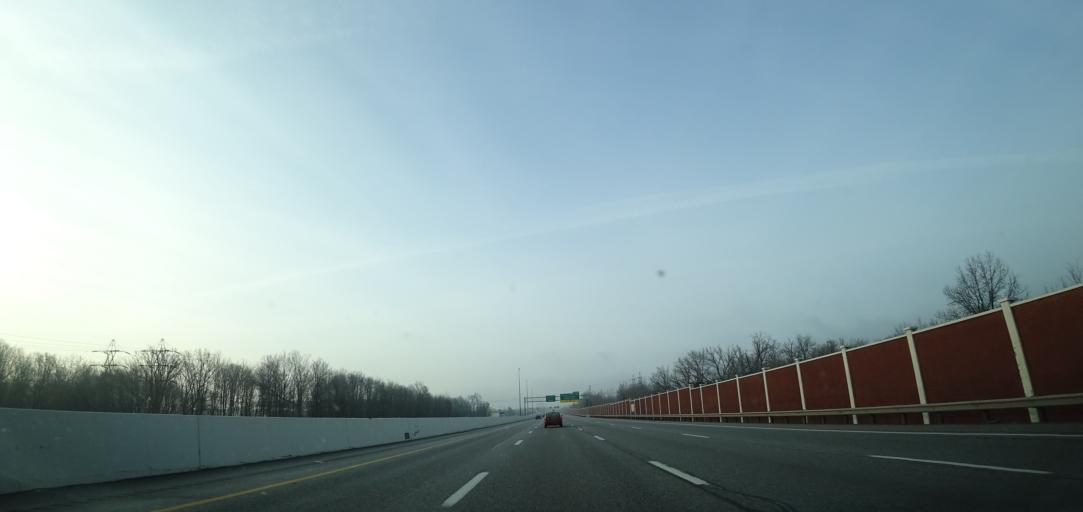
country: US
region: Ohio
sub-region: Cuyahoga County
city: Independence
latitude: 41.3689
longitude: -81.6515
